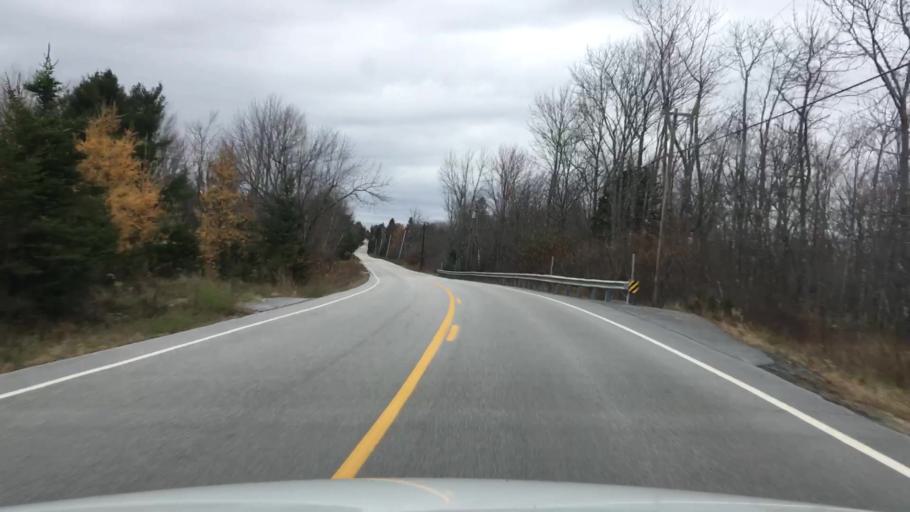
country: US
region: Maine
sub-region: Hancock County
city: Penobscot
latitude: 44.4683
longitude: -68.6359
